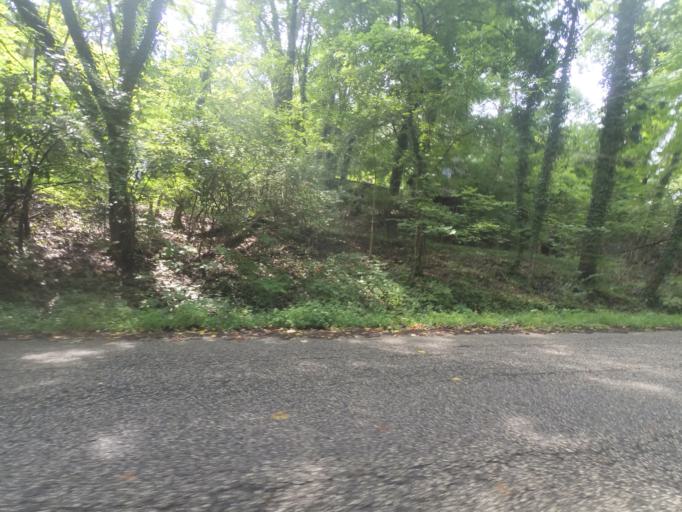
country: US
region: West Virginia
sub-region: Cabell County
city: Huntington
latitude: 38.4049
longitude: -82.4652
